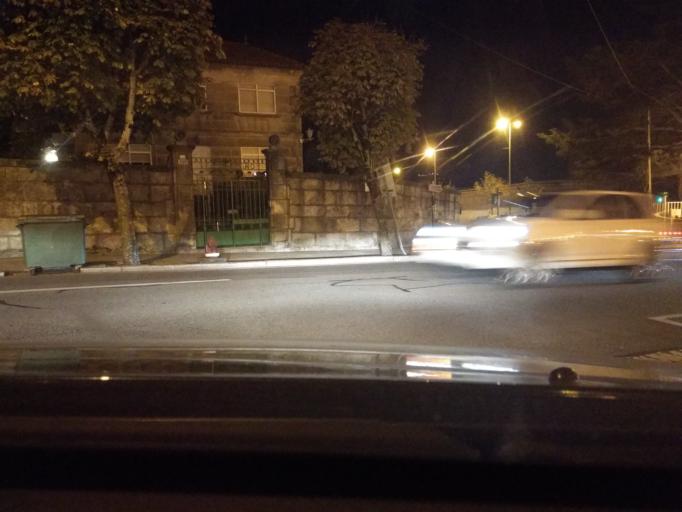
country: ES
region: Galicia
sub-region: Provincia de Pontevedra
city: Vigo
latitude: 42.2211
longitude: -8.7295
